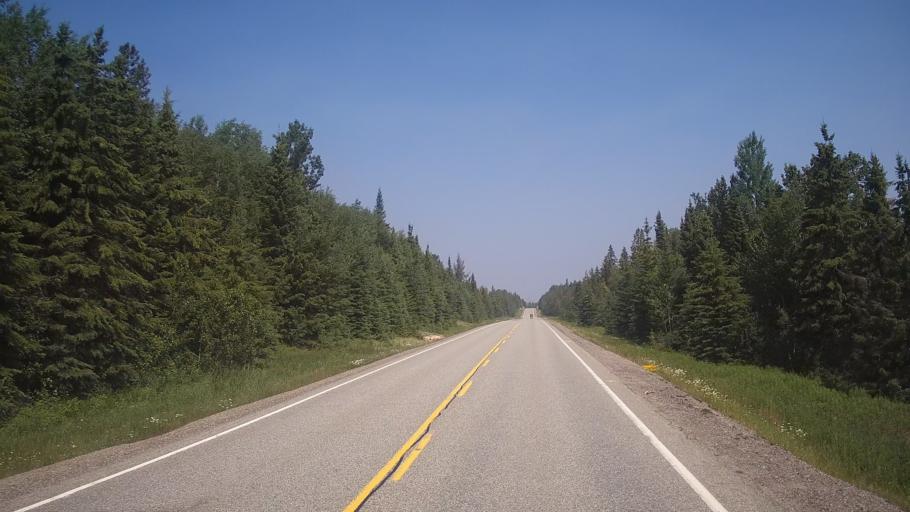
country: CA
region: Ontario
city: Timmins
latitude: 48.0368
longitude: -81.5827
